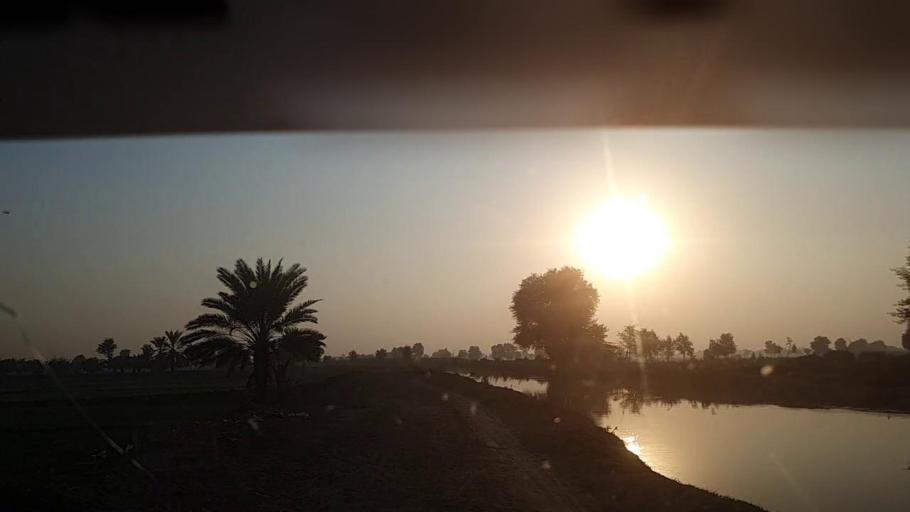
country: PK
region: Sindh
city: Ranipur
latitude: 27.2287
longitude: 68.5451
